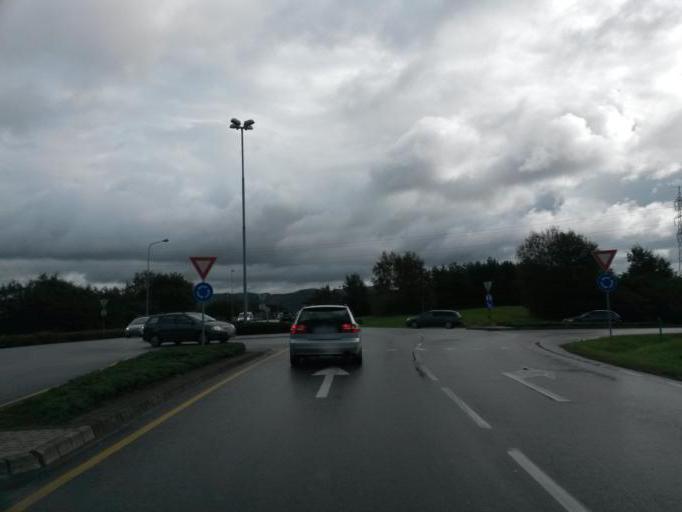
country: NO
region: Rogaland
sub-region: Sandnes
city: Sandnes
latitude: 58.8865
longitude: 5.7154
